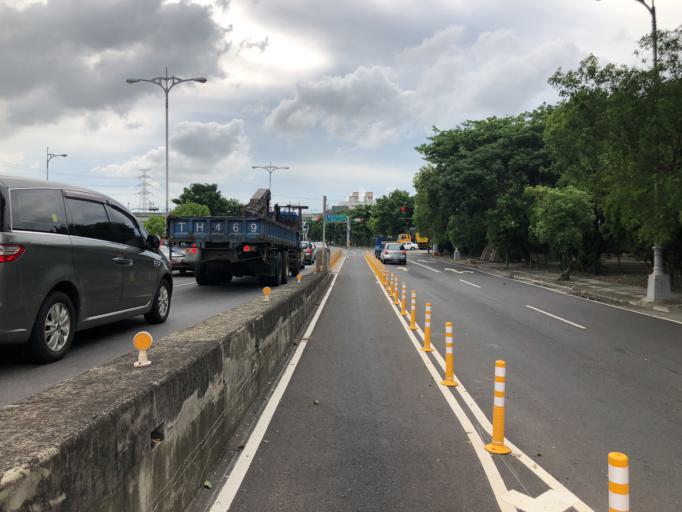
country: TW
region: Taiwan
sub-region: Changhua
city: Chang-hua
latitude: 24.1025
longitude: 120.6196
